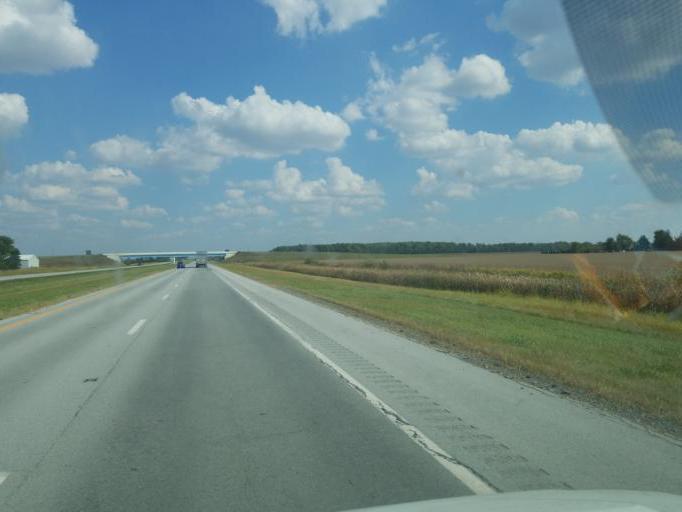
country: US
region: Ohio
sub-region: Allen County
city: Delphos
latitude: 40.8733
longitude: -84.4023
